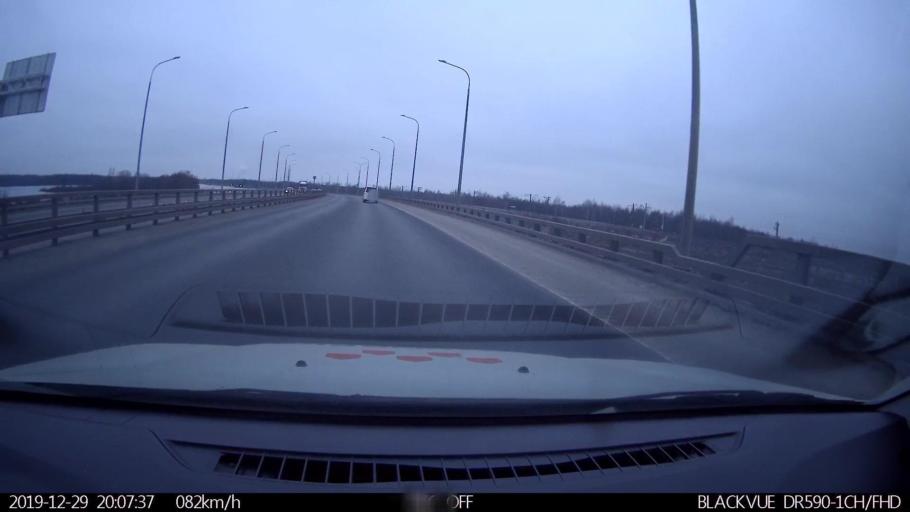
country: RU
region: Nizjnij Novgorod
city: Neklyudovo
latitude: 56.3925
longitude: 43.9805
